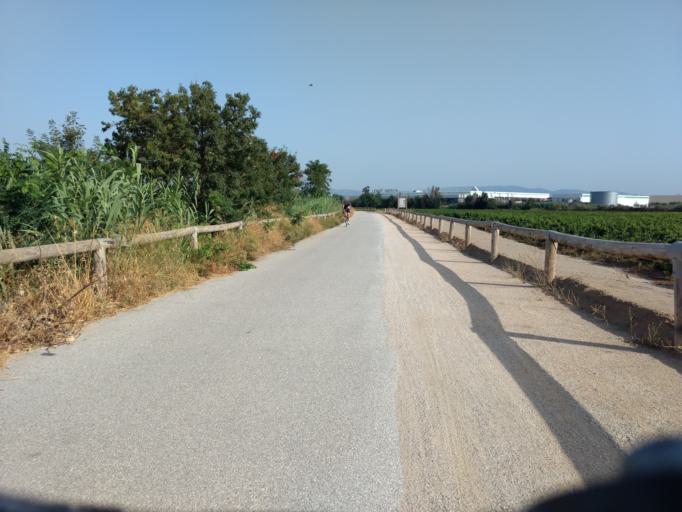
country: FR
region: Languedoc-Roussillon
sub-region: Departement des Pyrenees-Orientales
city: Pia
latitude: 42.7691
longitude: 2.9109
